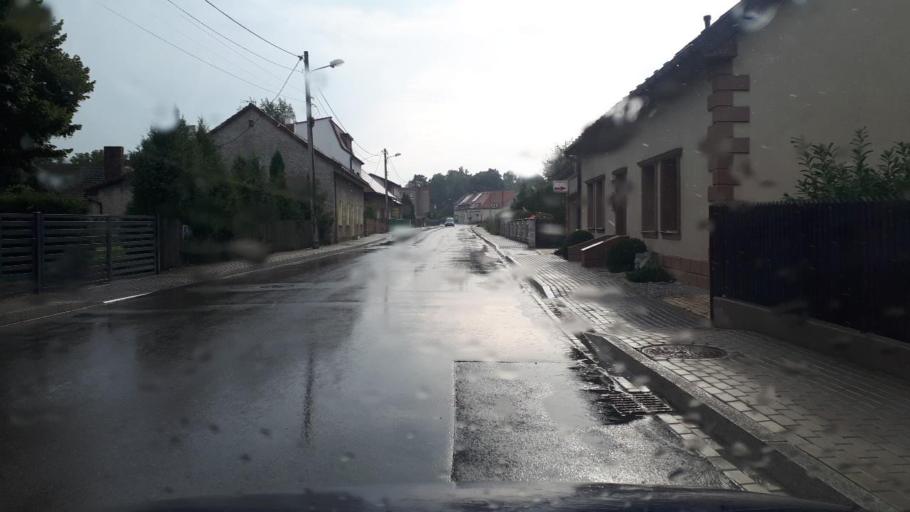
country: PL
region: Silesian Voivodeship
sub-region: Powiat gliwicki
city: Wielowies
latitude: 50.5071
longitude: 18.6118
